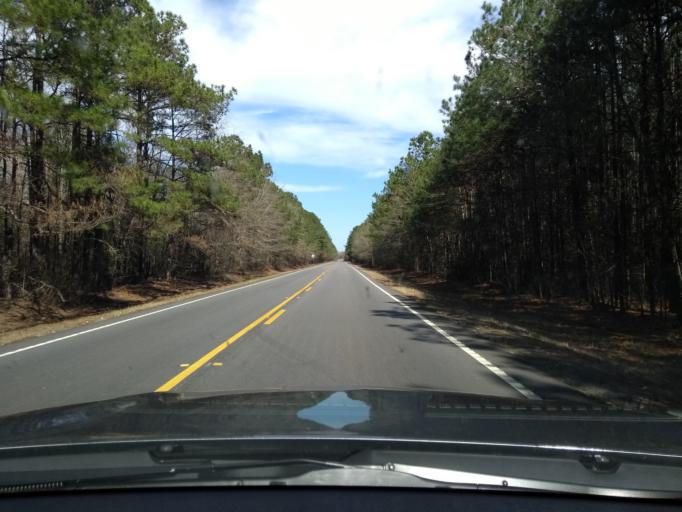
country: US
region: Georgia
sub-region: Bulloch County
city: Brooklet
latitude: 32.4847
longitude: -81.5745
